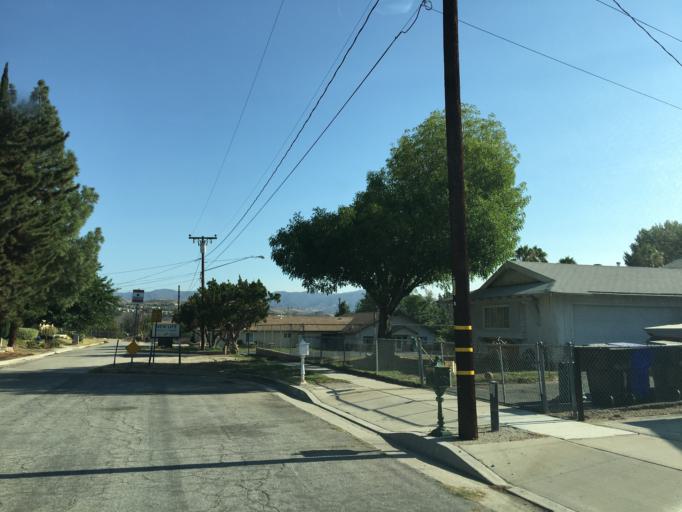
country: US
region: California
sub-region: Los Angeles County
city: Castaic
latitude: 34.4898
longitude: -118.6229
